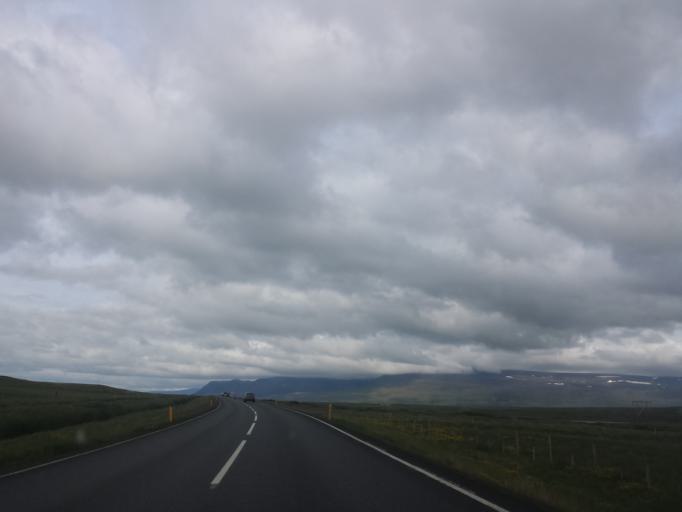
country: IS
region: Northwest
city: Saudarkrokur
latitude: 65.3461
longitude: -20.7758
